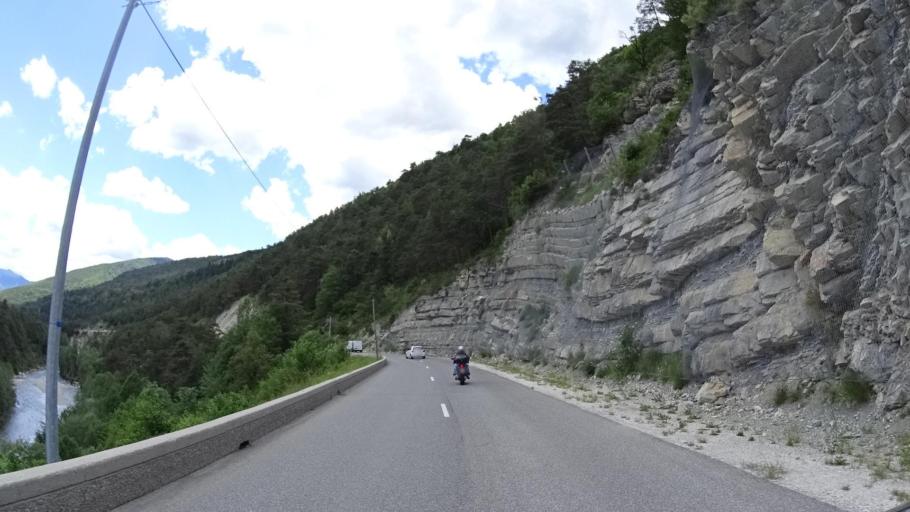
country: FR
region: Provence-Alpes-Cote d'Azur
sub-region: Departement des Alpes-de-Haute-Provence
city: Annot
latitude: 44.0281
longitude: 6.5543
